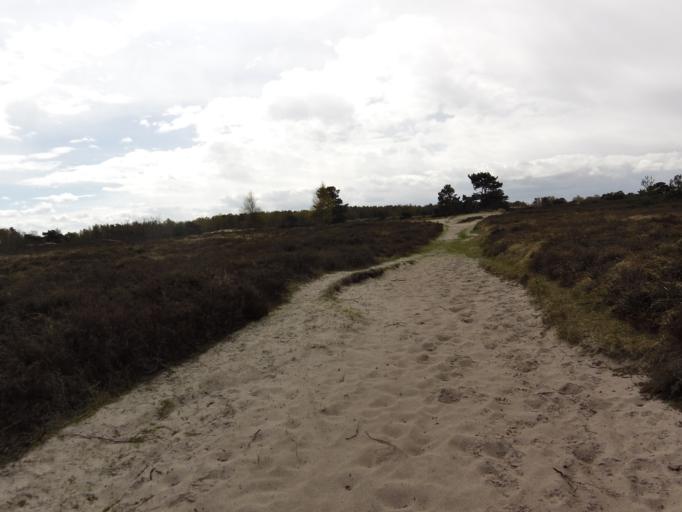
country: DE
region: Mecklenburg-Vorpommern
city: Hiddensee
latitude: 54.5450
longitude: 13.0981
